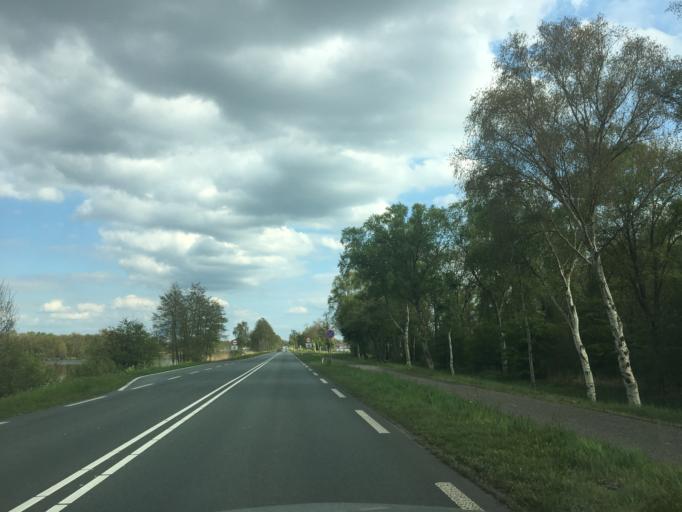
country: NL
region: North Holland
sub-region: Gemeente Wijdemeren
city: Oud-Loosdrecht
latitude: 52.2329
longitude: 5.0666
